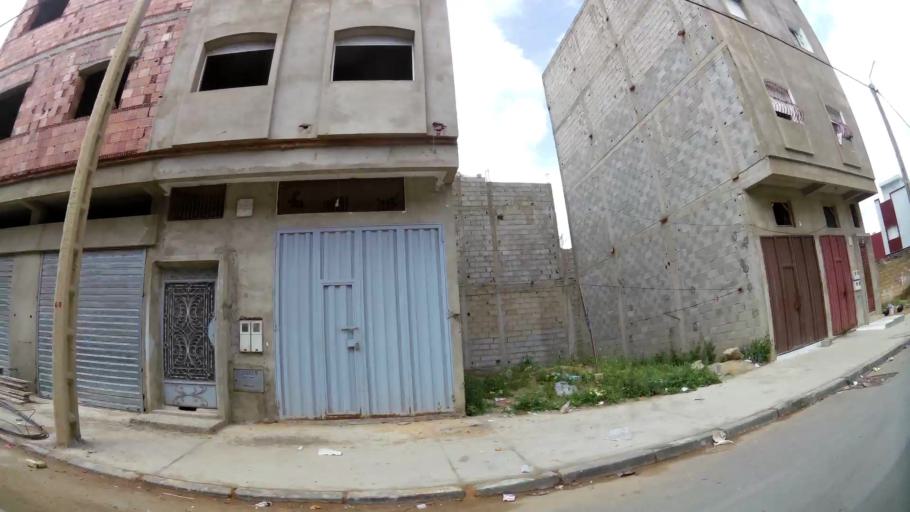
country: MA
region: Rabat-Sale-Zemmour-Zaer
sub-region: Khemisset
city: Tiflet
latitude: 33.8903
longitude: -6.3259
